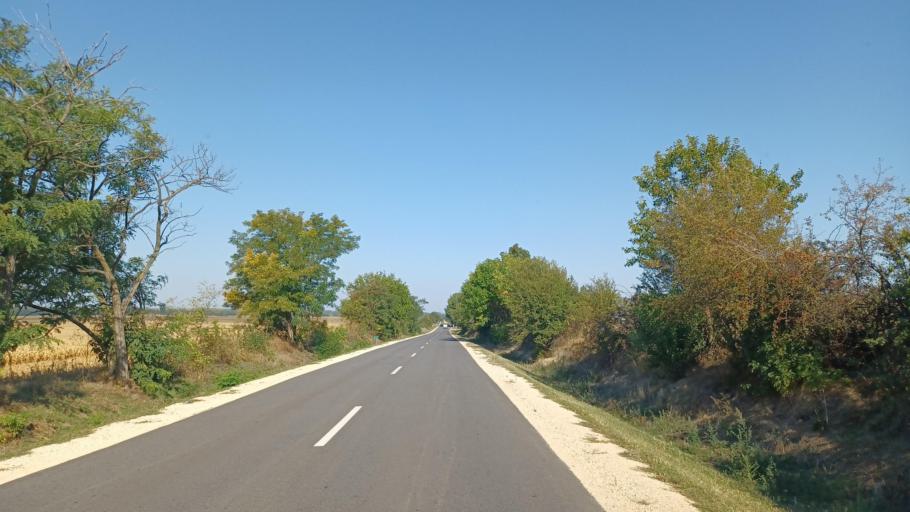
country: HU
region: Tolna
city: Paks
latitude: 46.6528
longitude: 18.8383
